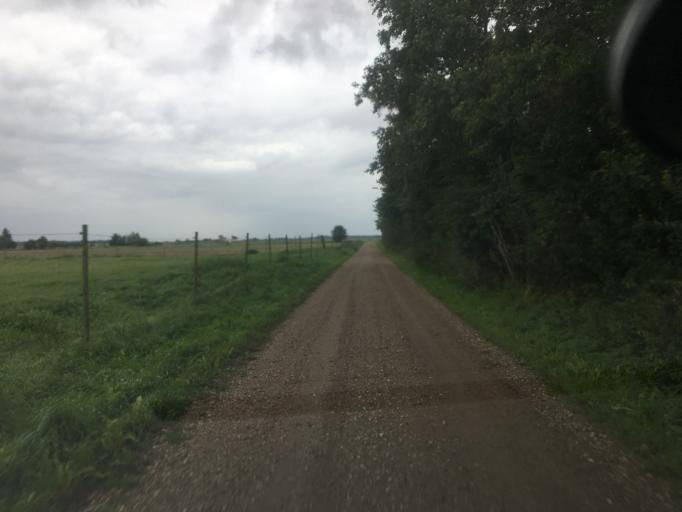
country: DK
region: South Denmark
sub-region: Tonder Kommune
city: Tonder
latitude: 54.9766
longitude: 8.9314
